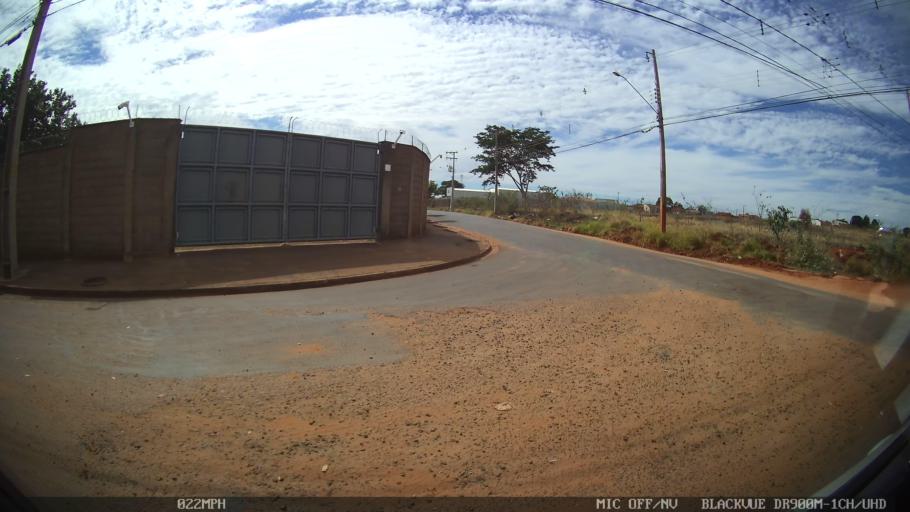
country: BR
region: Sao Paulo
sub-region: Catanduva
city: Catanduva
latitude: -21.1593
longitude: -48.9760
